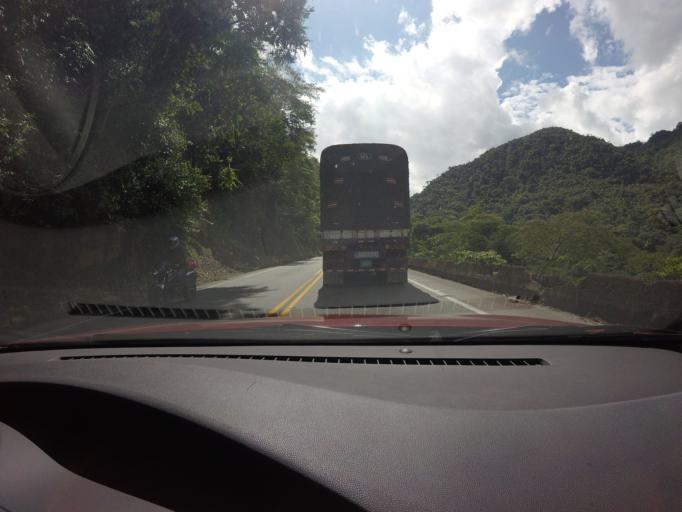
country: CO
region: Antioquia
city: San Luis
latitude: 5.9940
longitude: -74.9388
